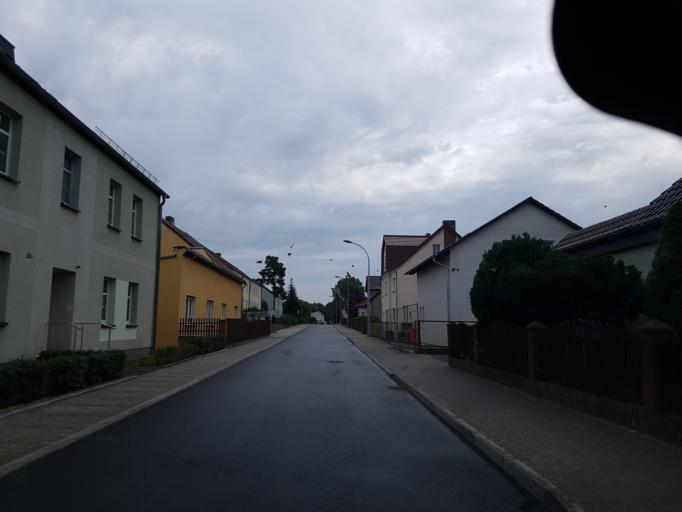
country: DE
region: Brandenburg
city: Senftenberg
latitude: 51.5261
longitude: 13.9466
